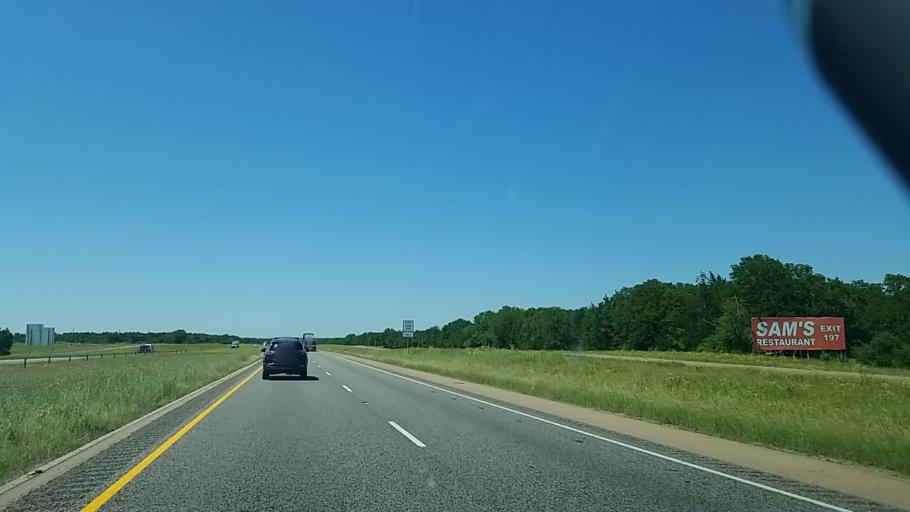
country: US
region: Texas
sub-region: Freestone County
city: Fairfield
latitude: 31.6052
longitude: -96.1561
